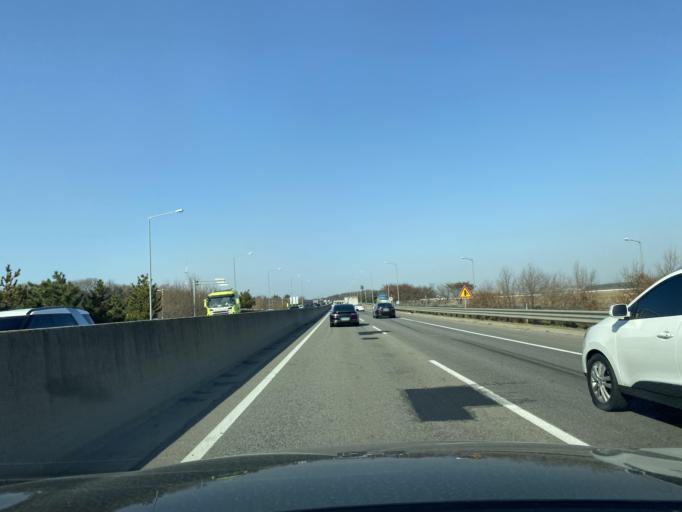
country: KR
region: Gyeonggi-do
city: Hwaseong-si
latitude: 37.2398
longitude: 126.7583
